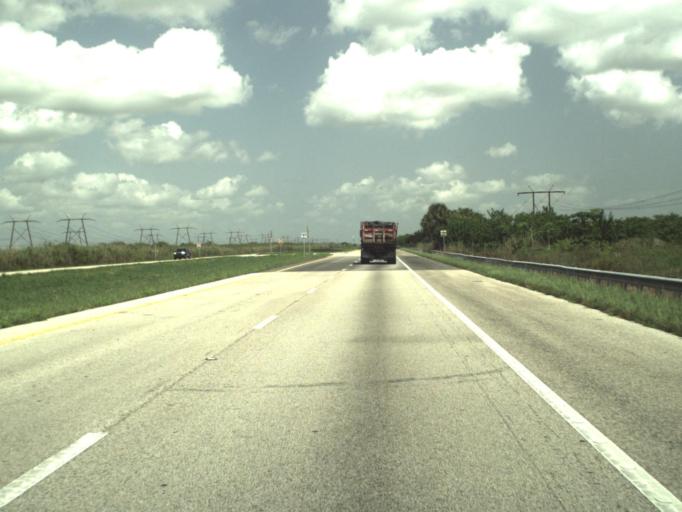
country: US
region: Florida
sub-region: Broward County
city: Weston
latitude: 26.2684
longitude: -80.4863
